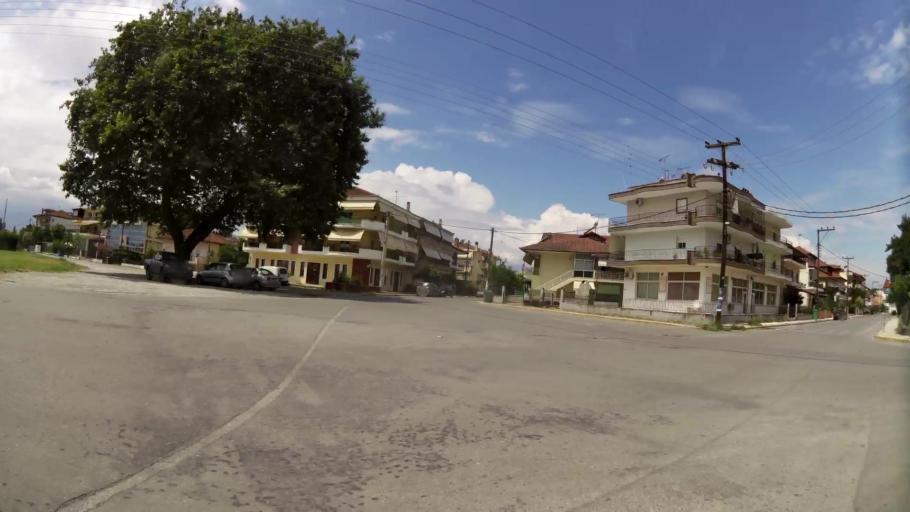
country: GR
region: Central Macedonia
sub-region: Nomos Pierias
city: Katerini
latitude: 40.2617
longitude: 22.5104
